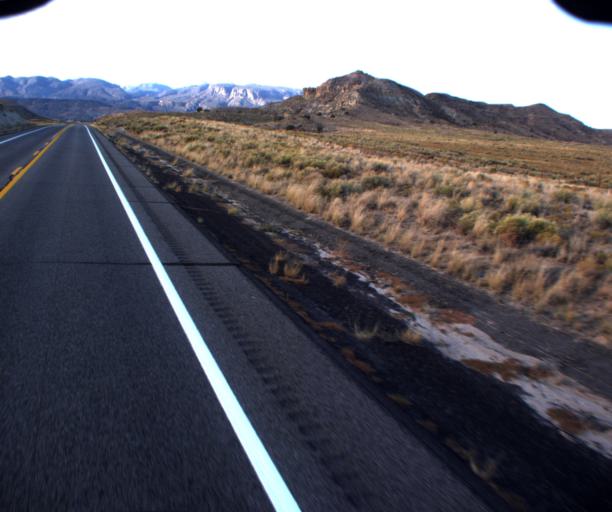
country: US
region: New Mexico
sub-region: San Juan County
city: Shiprock
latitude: 36.9485
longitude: -109.0721
